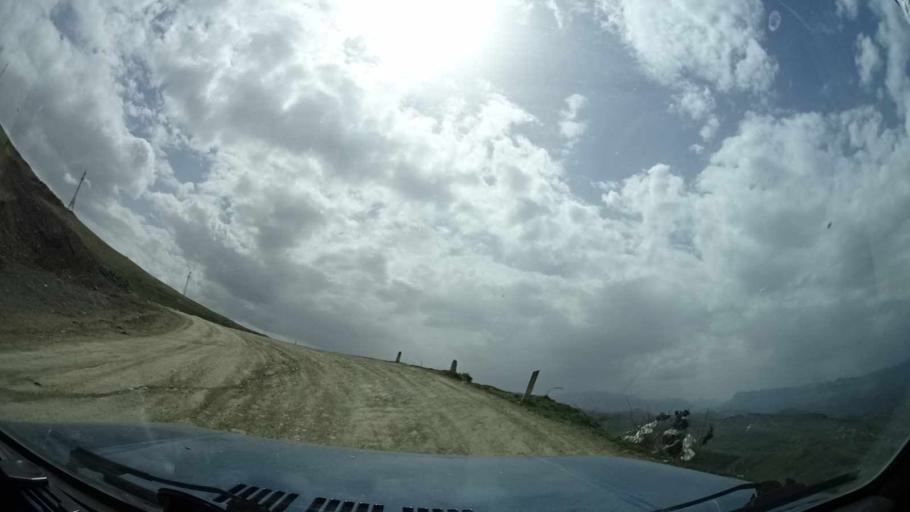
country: RU
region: Dagestan
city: Kubachi
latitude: 42.0891
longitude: 47.5804
